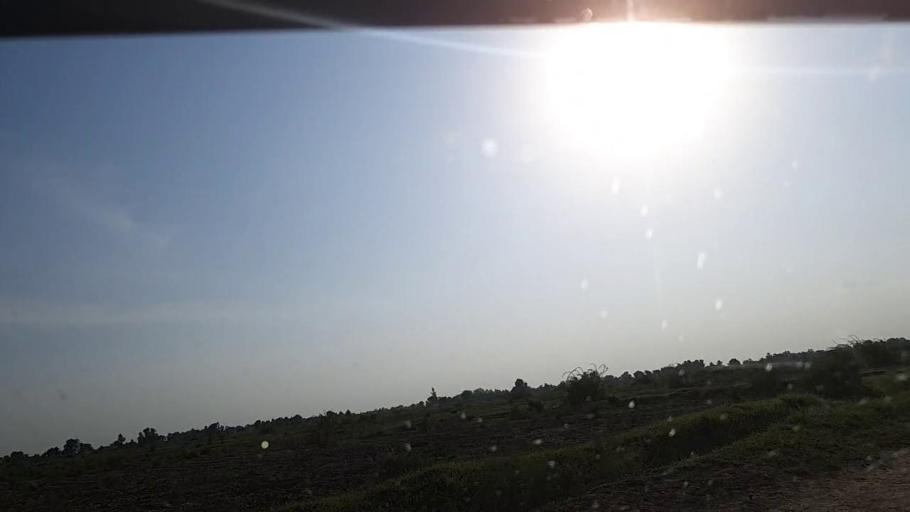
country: PK
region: Sindh
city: Pano Aqil
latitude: 27.9043
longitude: 69.2097
